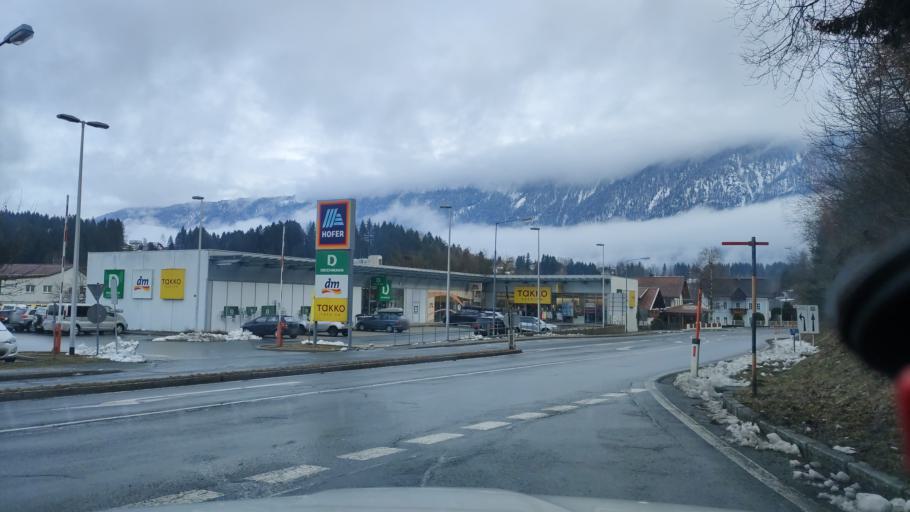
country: AT
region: Carinthia
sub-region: Politischer Bezirk Hermagor
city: Hermagor
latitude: 46.6246
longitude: 13.3721
